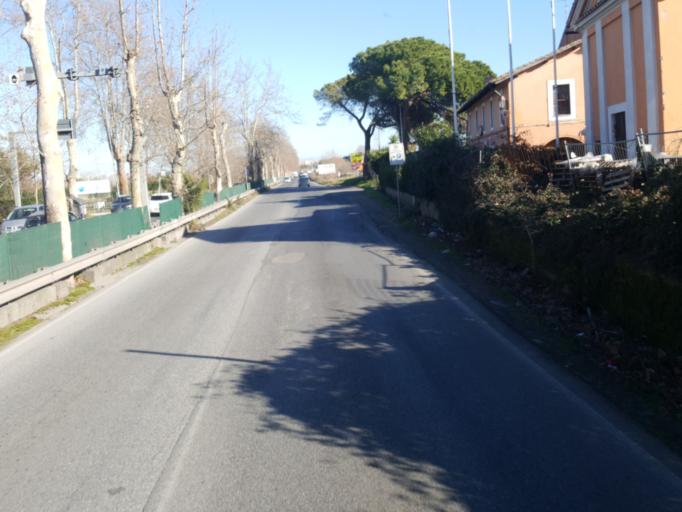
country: IT
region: Latium
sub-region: Citta metropolitana di Roma Capitale
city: Vitinia
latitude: 41.7924
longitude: 12.3879
